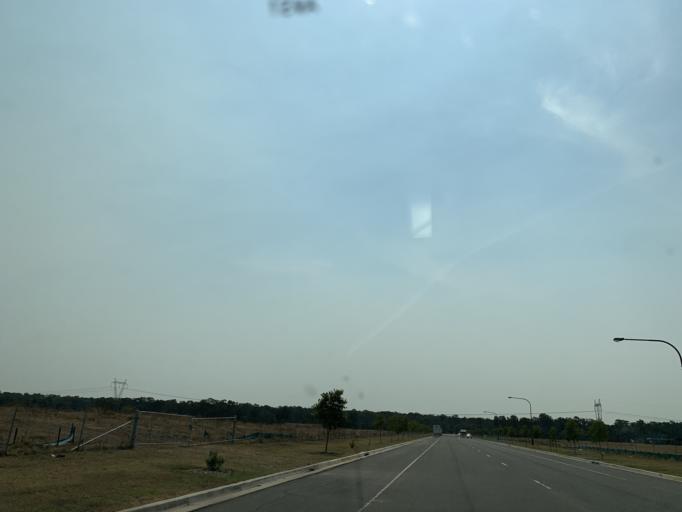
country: AU
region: New South Wales
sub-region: Blacktown
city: Hassall Grove
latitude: -33.7187
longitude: 150.8255
